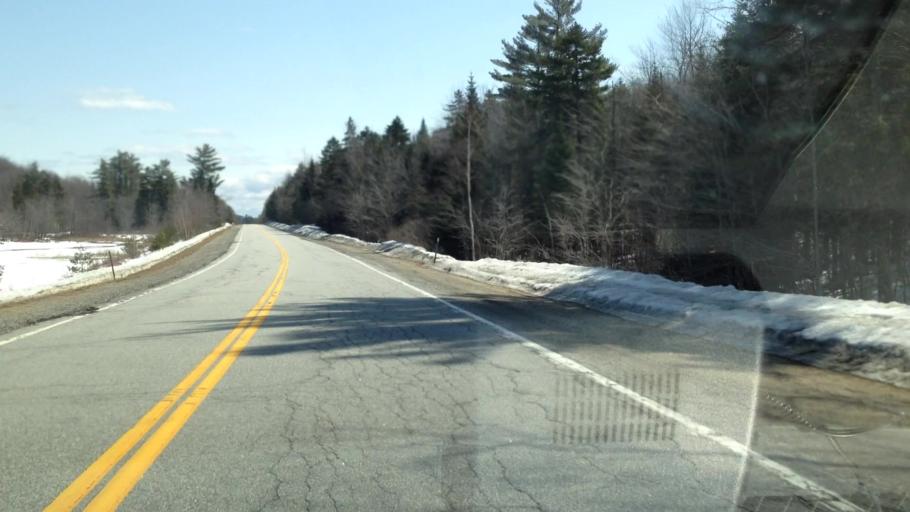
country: US
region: New Hampshire
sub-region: Sullivan County
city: Springfield
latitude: 43.4972
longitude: -72.0088
